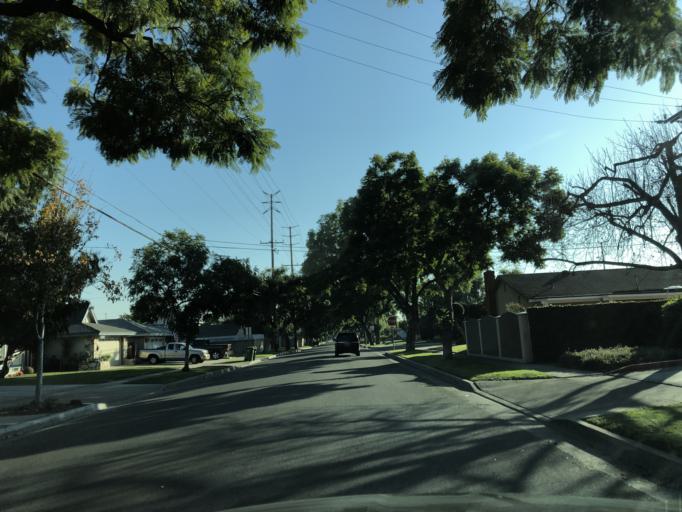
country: US
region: California
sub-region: Orange County
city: Orange
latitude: 33.7665
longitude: -117.8474
